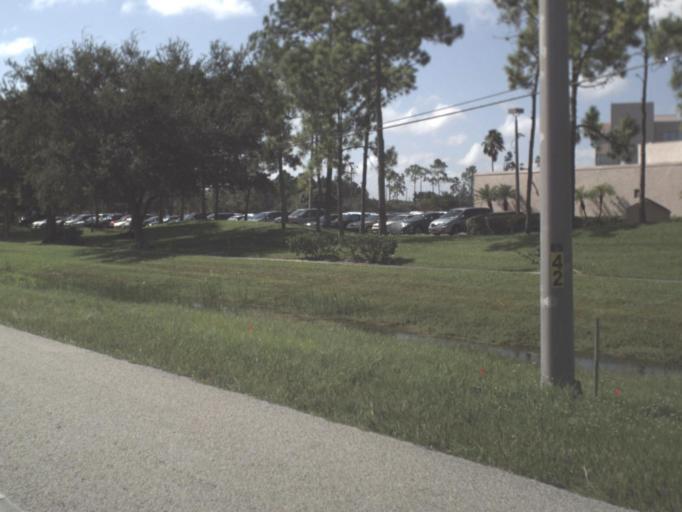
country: US
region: Florida
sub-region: Pinellas County
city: Gandy
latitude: 27.8707
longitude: -82.6483
